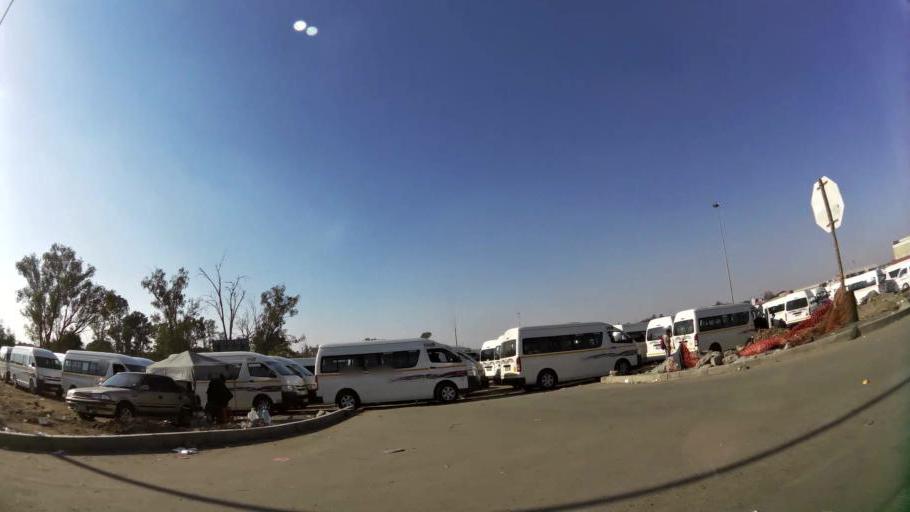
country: ZA
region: North-West
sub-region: Bojanala Platinum District Municipality
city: Rustenburg
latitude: -25.6632
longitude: 27.2341
